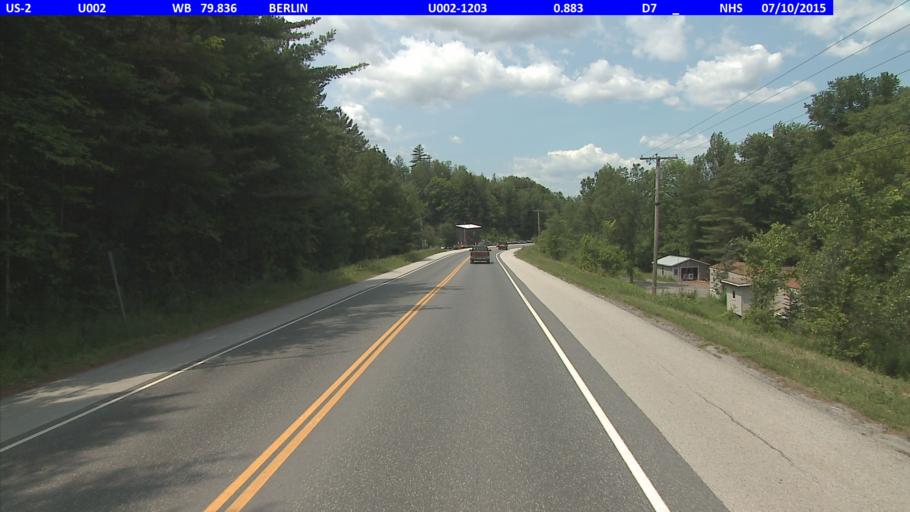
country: US
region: Vermont
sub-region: Washington County
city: Barre
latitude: 44.2377
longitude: -72.5276
